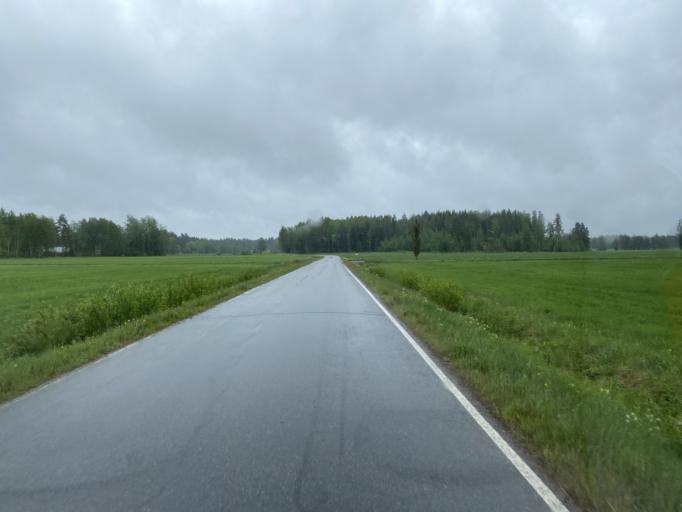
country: FI
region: Haeme
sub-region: Forssa
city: Humppila
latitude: 61.0511
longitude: 23.3491
